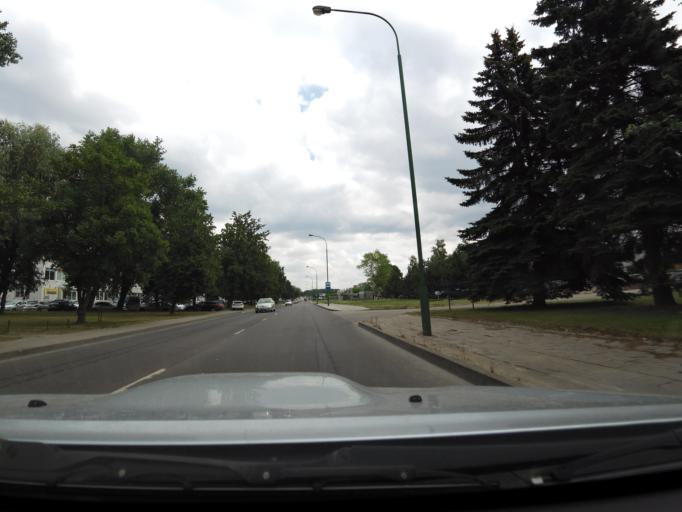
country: LT
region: Klaipedos apskritis
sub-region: Klaipeda
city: Klaipeda
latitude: 55.6915
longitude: 21.1652
